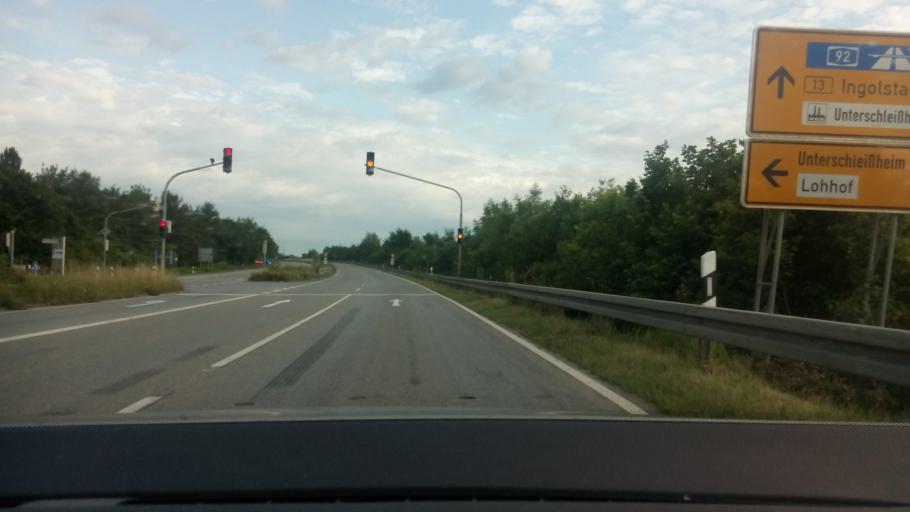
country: DE
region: Bavaria
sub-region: Upper Bavaria
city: Unterschleissheim
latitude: 48.2868
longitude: 11.5886
